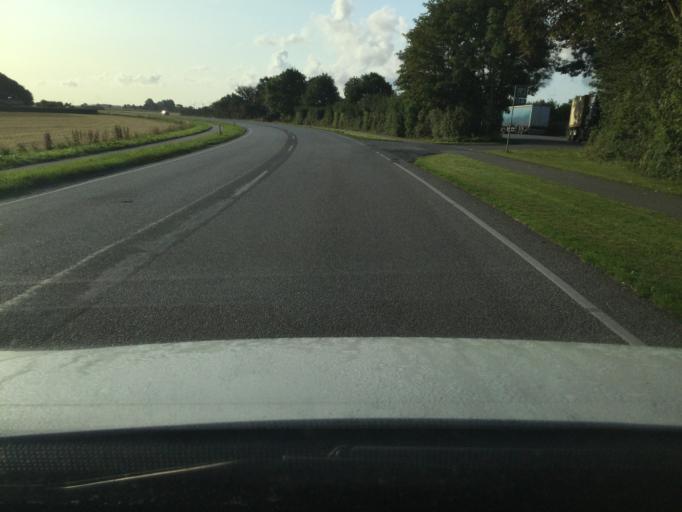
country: DK
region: Zealand
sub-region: Lolland Kommune
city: Nakskov
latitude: 54.8146
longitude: 11.1614
